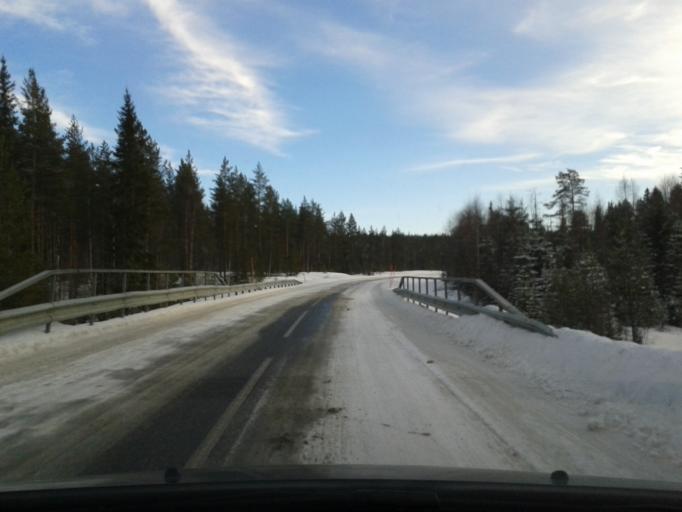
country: SE
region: Vaesterbotten
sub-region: Asele Kommun
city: Asele
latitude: 64.2757
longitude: 17.2724
